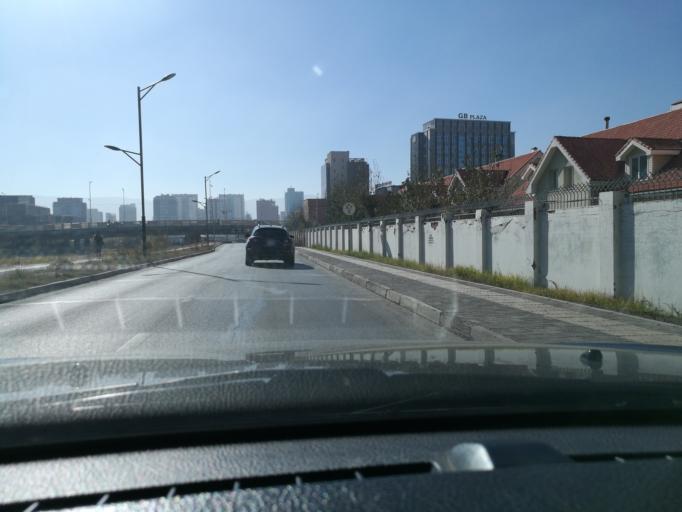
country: MN
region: Ulaanbaatar
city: Ulaanbaatar
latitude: 47.9245
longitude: 106.9313
